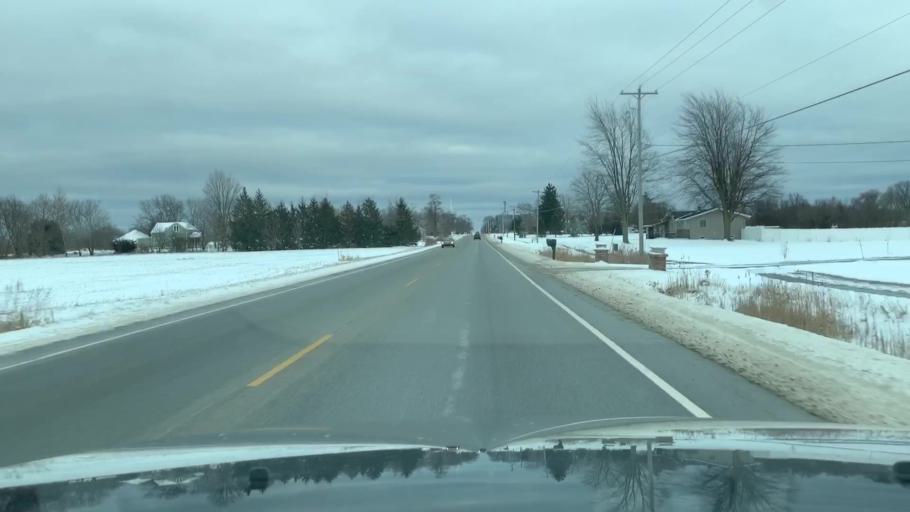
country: US
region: Michigan
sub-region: Ottawa County
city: Zeeland
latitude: 42.8120
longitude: -85.9492
